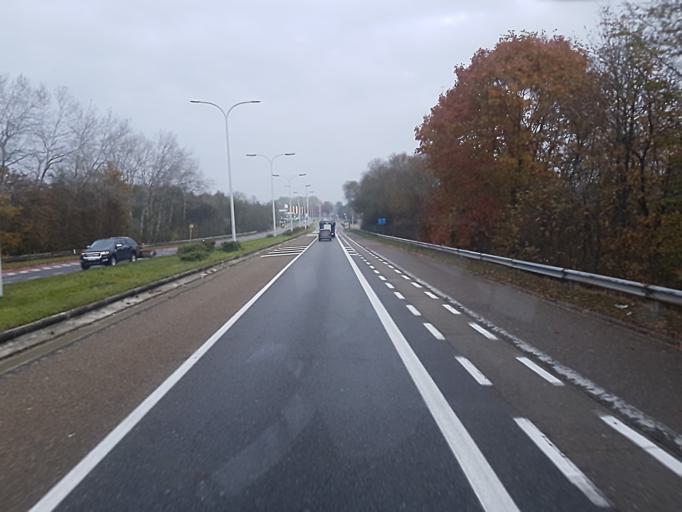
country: BE
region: Flanders
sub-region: Provincie Antwerpen
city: Vosselaar
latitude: 51.2991
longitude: 4.9143
